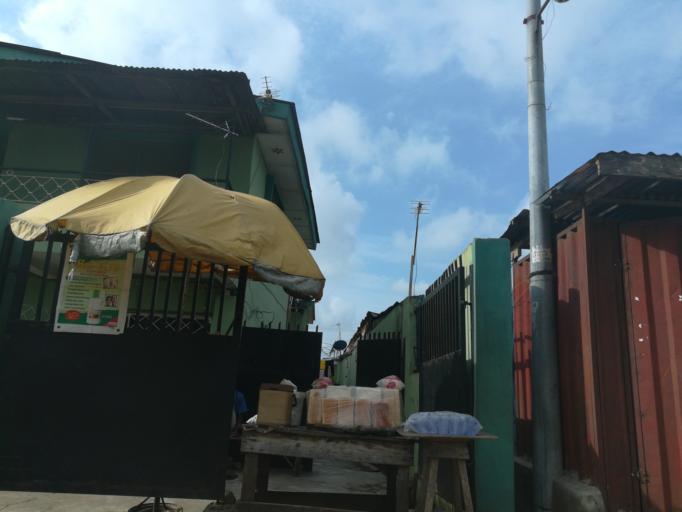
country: NG
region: Lagos
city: Agege
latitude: 6.6138
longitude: 3.3223
